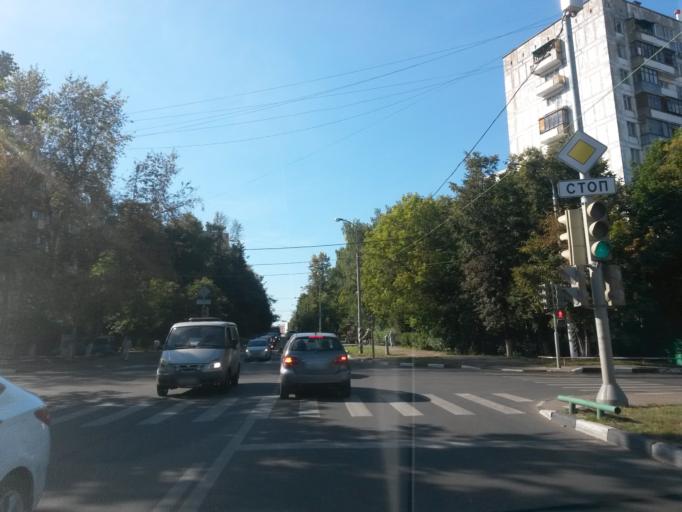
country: RU
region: Moscow
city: Kotlovka
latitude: 55.6605
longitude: 37.5889
